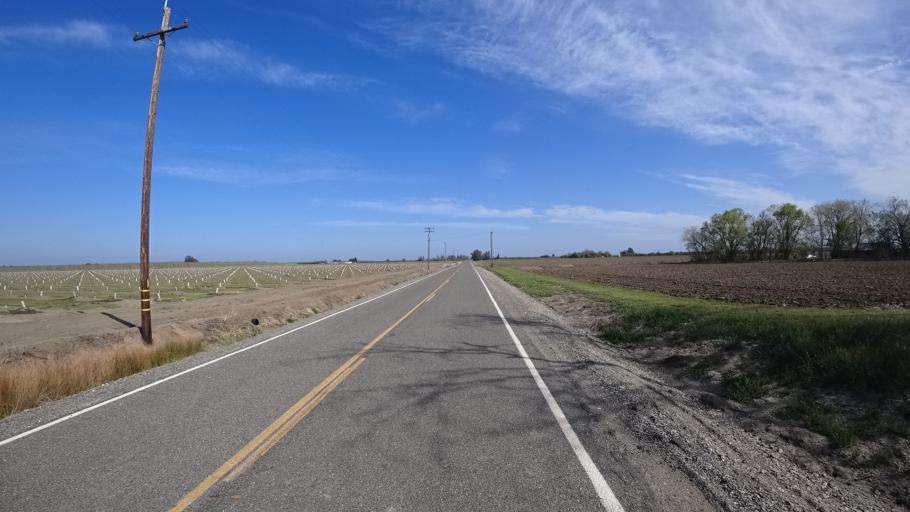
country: US
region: California
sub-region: Glenn County
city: Hamilton City
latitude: 39.6162
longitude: -122.0368
